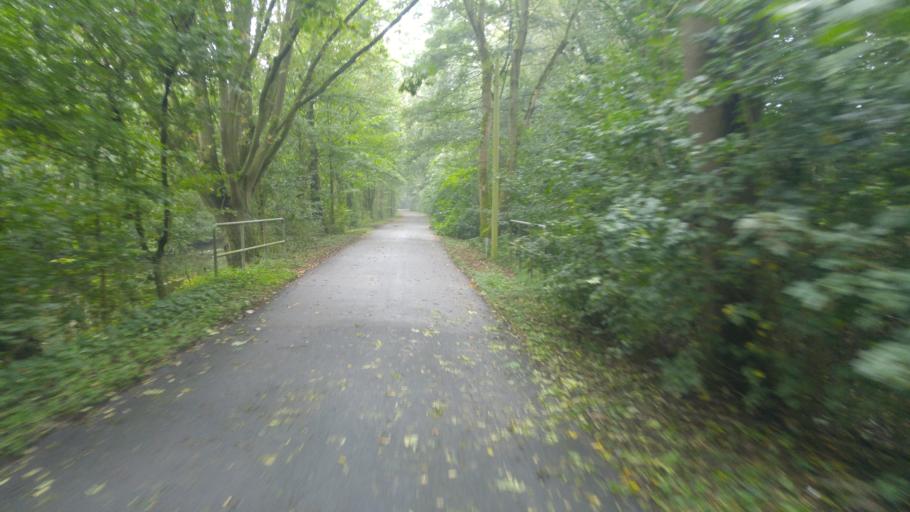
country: DE
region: Bremen
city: Bremen
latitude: 53.1077
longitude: 8.8357
